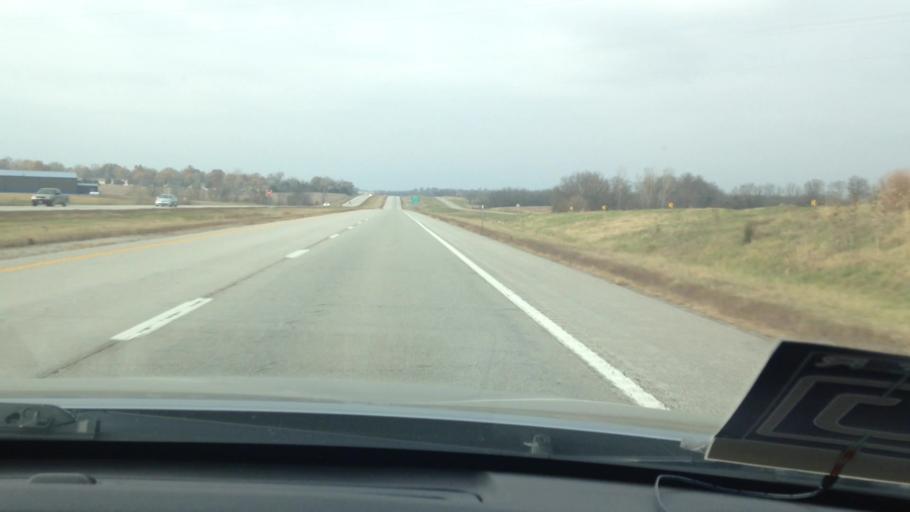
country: US
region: Missouri
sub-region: Cass County
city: Garden City
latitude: 38.5550
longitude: -94.1788
